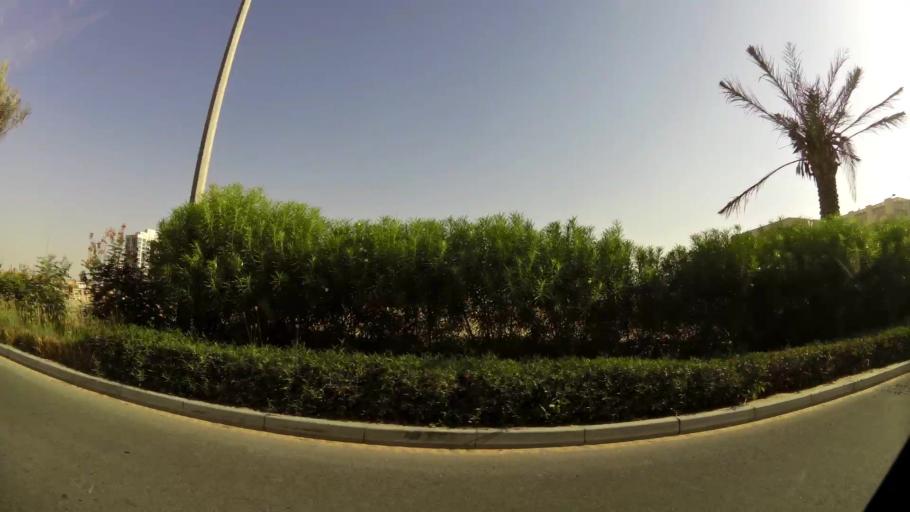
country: AE
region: Dubai
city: Dubai
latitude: 25.0459
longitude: 55.2037
